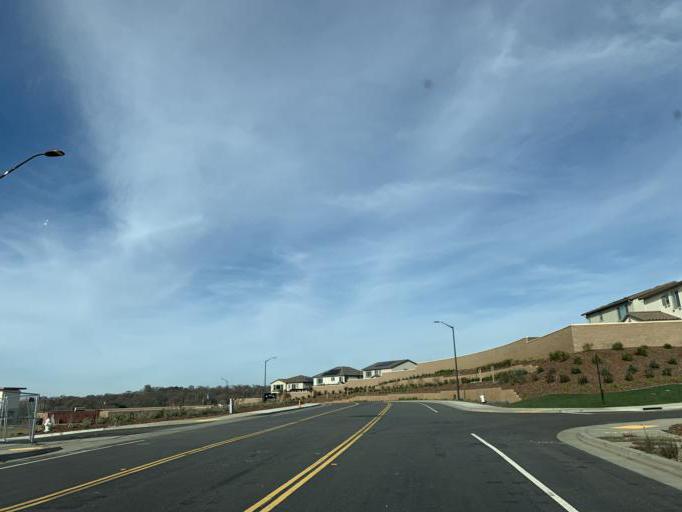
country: US
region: California
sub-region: El Dorado County
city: Cameron Park
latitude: 38.6745
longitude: -121.0264
